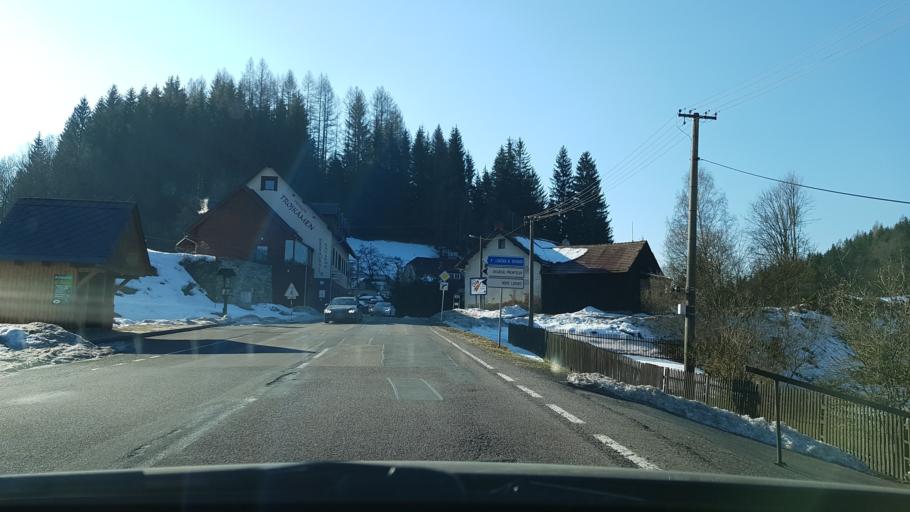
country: CZ
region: Olomoucky
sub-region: Okres Sumperk
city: Stare Mesto
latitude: 50.1156
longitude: 17.0066
